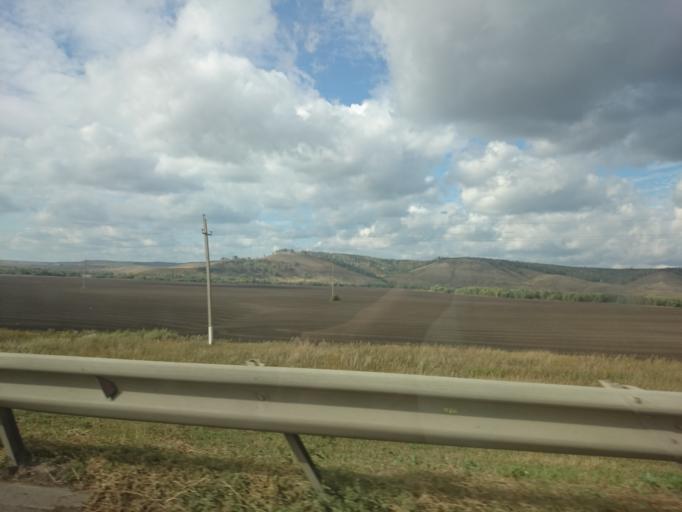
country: RU
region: Samara
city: Kamyshla
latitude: 54.0727
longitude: 52.2194
